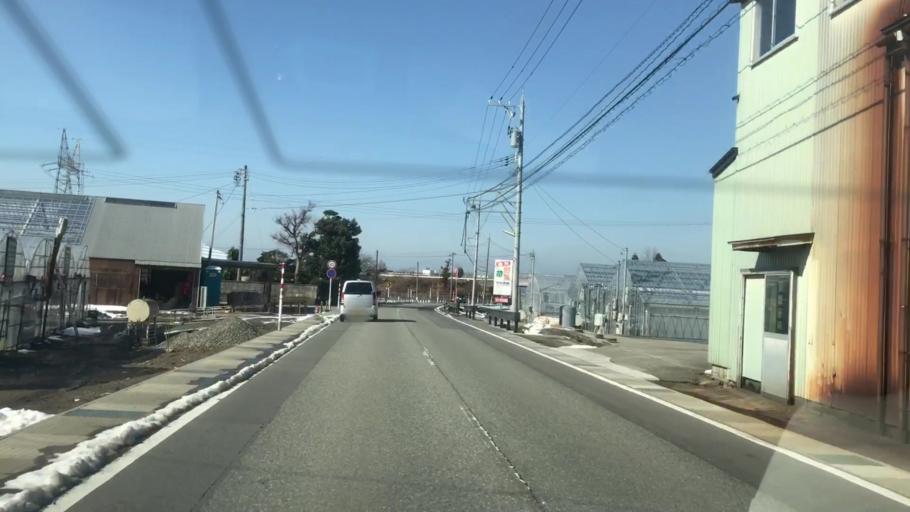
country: JP
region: Toyama
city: Toyama-shi
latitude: 36.6476
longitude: 137.2483
